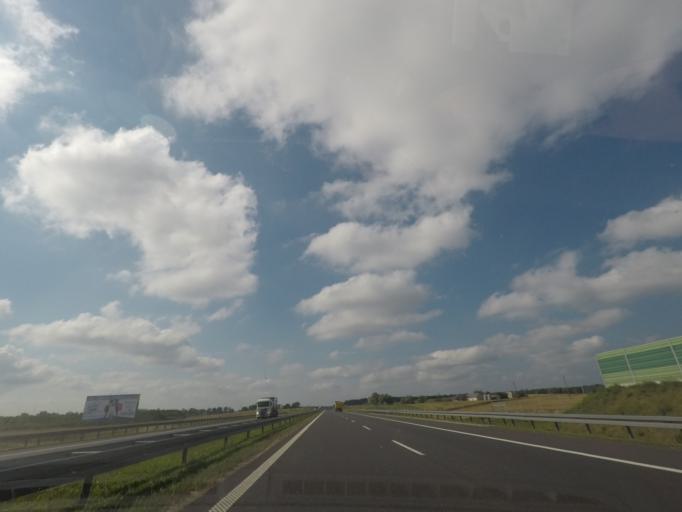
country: PL
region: Kujawsko-Pomorskie
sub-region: Powiat swiecki
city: Warlubie
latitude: 53.5886
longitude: 18.6118
